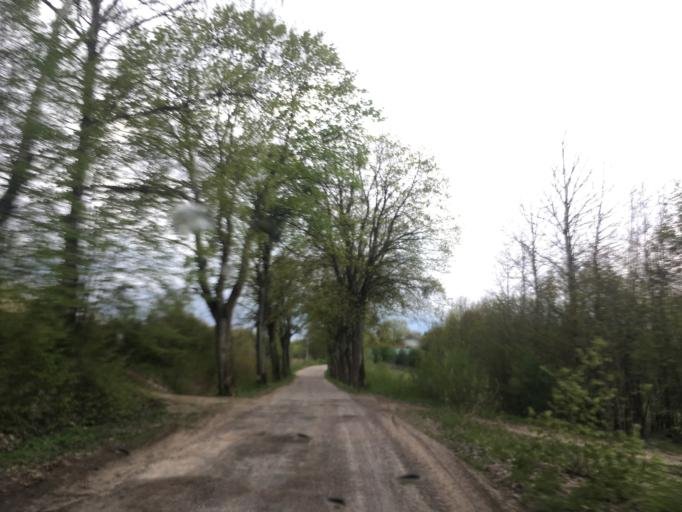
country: PL
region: Warmian-Masurian Voivodeship
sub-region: Powiat nidzicki
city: Kozlowo
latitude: 53.4219
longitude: 20.1893
